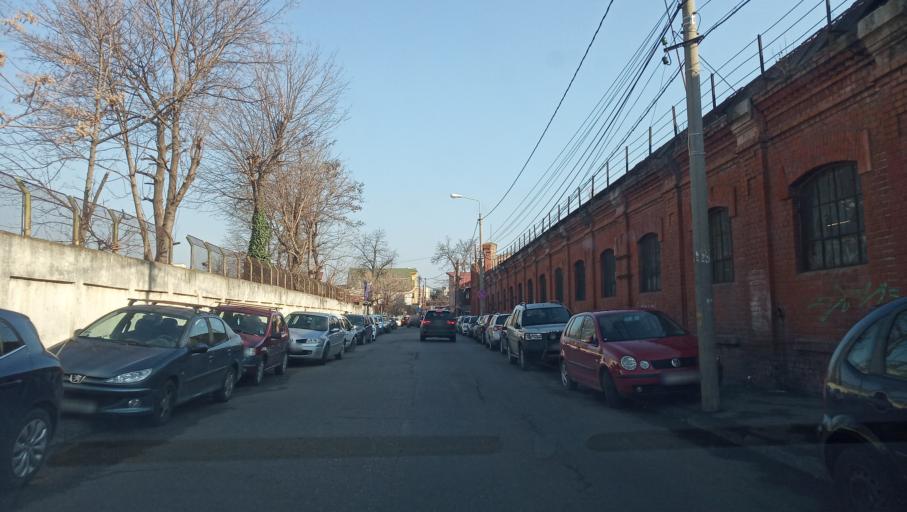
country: RO
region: Bucuresti
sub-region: Municipiul Bucuresti
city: Bucharest
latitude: 44.4548
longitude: 26.1155
